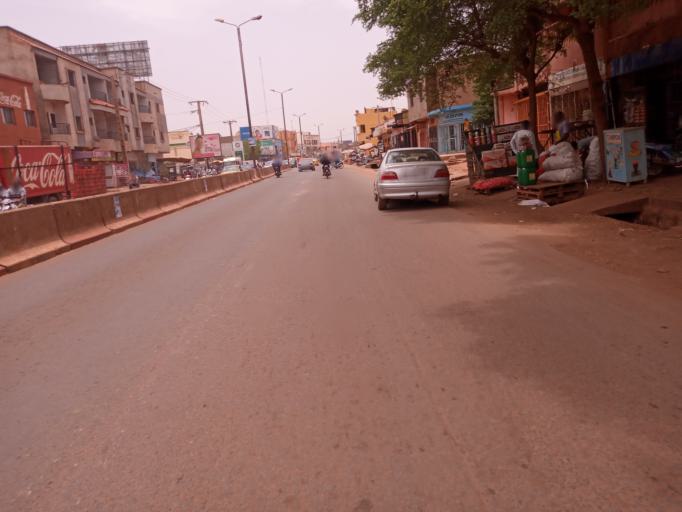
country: ML
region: Bamako
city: Bamako
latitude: 12.5995
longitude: -8.0131
